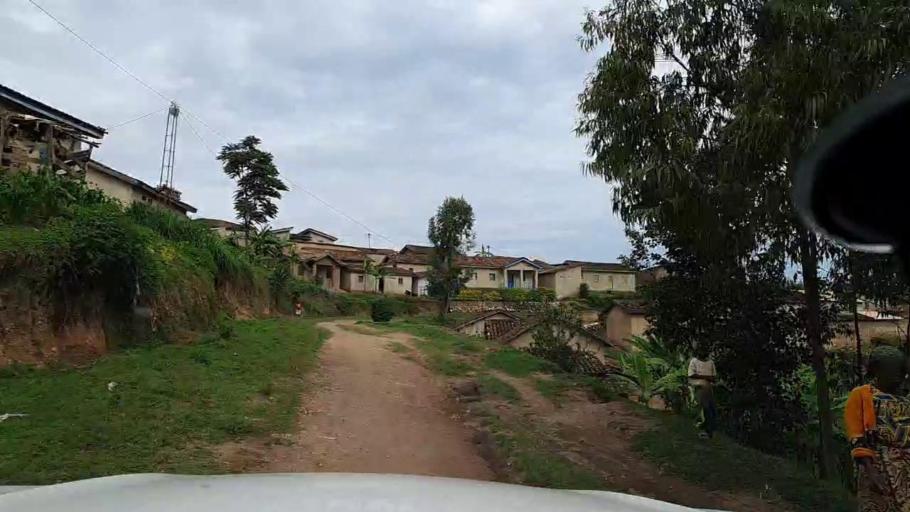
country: RW
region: Southern Province
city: Gitarama
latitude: -2.1276
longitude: 29.6552
